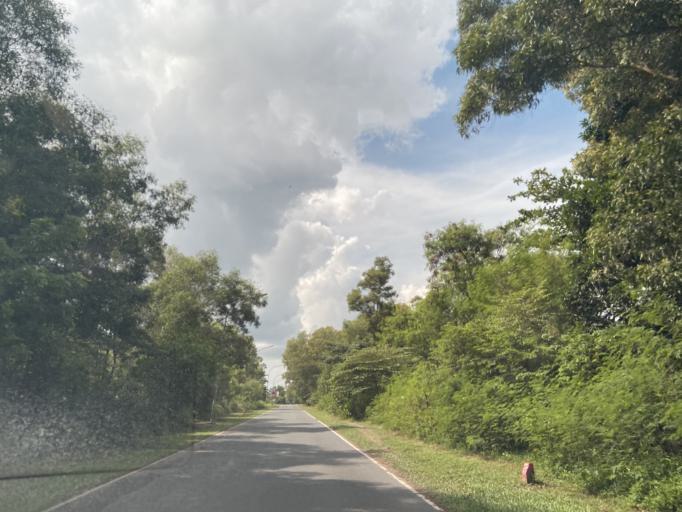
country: SG
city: Singapore
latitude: 1.1091
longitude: 104.0298
